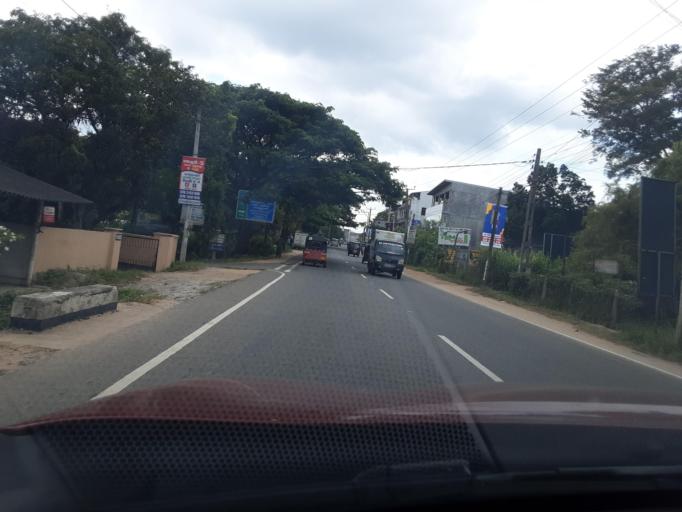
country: LK
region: North Western
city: Kurunegala
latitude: 7.4340
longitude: 80.2117
